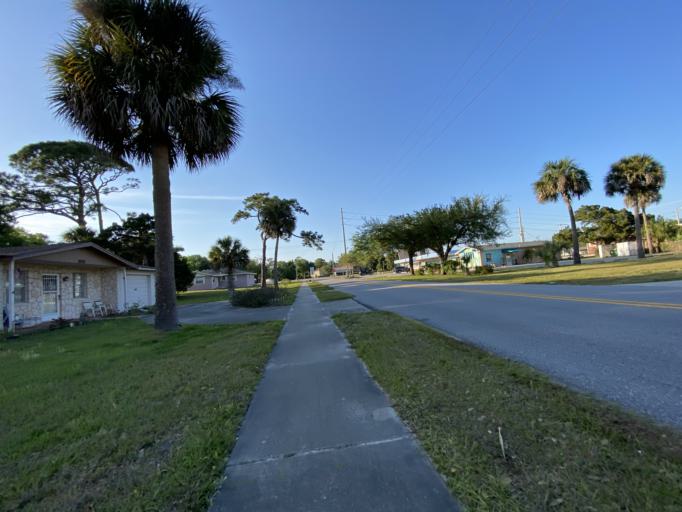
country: US
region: Florida
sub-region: Volusia County
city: South Daytona
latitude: 29.1717
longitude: -81.0071
